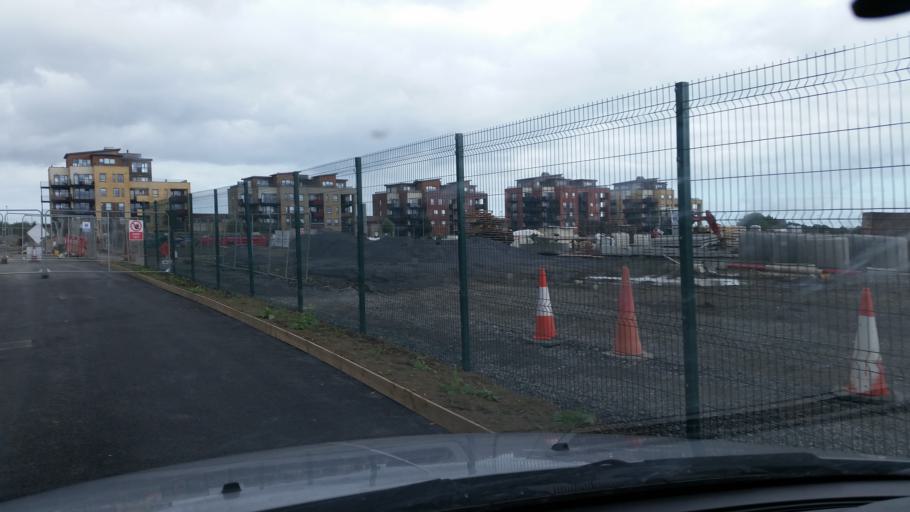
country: IE
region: Leinster
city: Donaghmede
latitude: 53.4061
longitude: -6.1562
